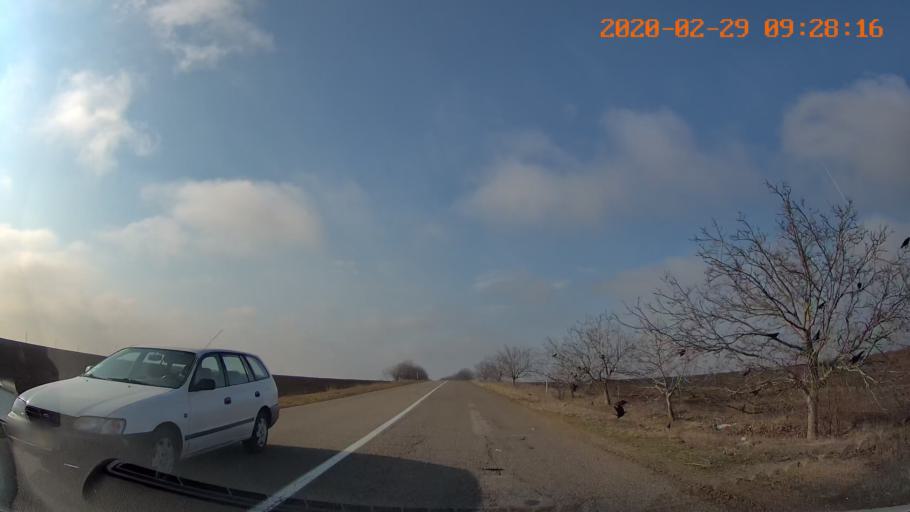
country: UA
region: Odessa
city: Lymanske
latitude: 46.6909
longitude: 29.9313
